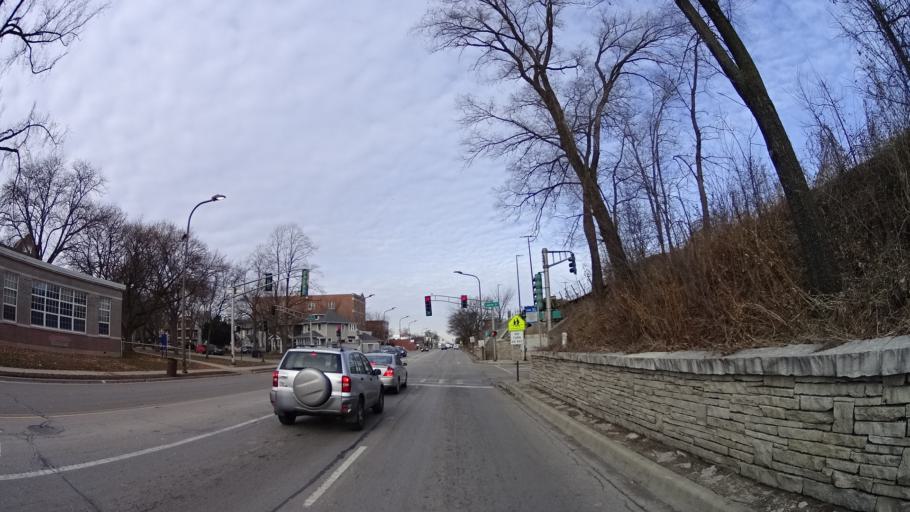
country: US
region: Illinois
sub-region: Cook County
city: Evanston
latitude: 42.0620
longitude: -87.6967
